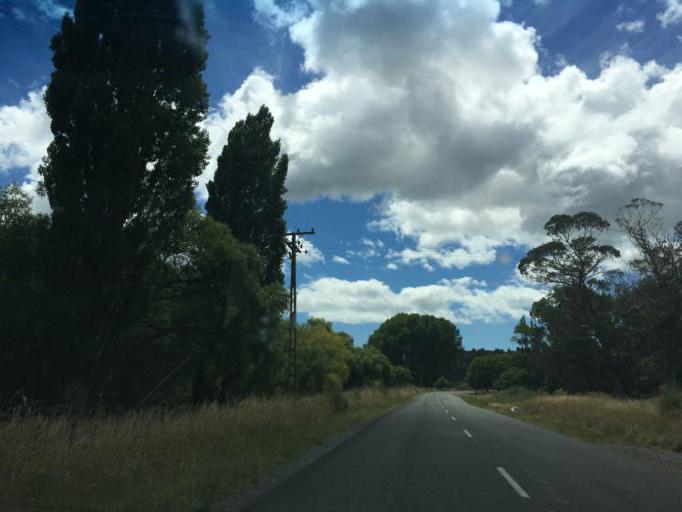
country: NZ
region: Hawke's Bay
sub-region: Hastings District
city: Hastings
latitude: -39.7488
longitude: 176.8791
